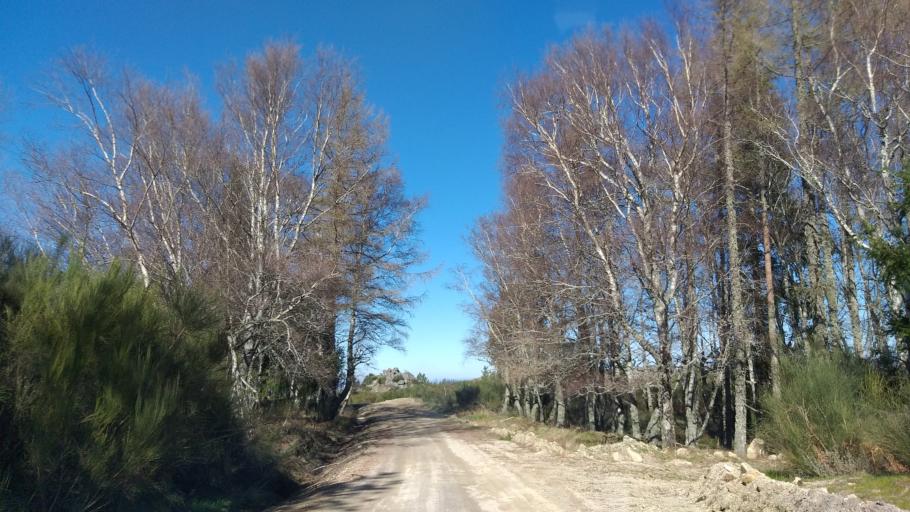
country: PT
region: Guarda
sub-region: Manteigas
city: Manteigas
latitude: 40.4940
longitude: -7.4924
